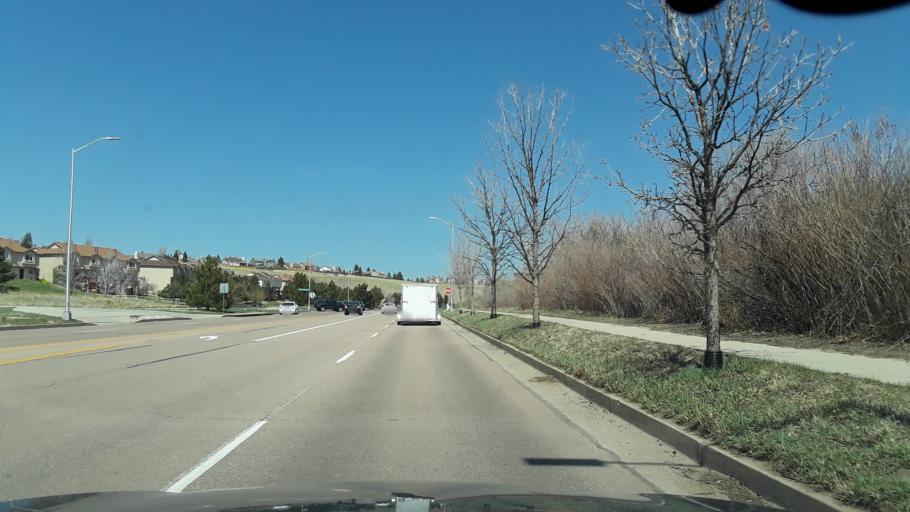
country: US
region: Colorado
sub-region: El Paso County
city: Black Forest
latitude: 38.9447
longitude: -104.7421
